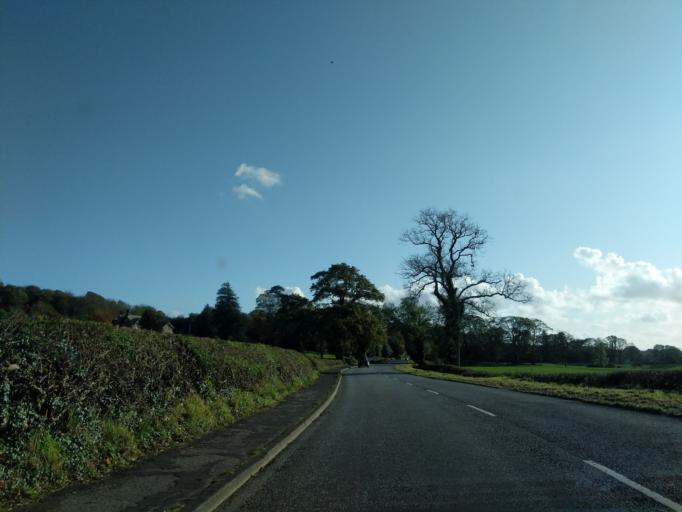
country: GB
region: Scotland
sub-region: Dumfries and Galloway
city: Kirkcudbright
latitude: 54.8540
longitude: -4.0402
